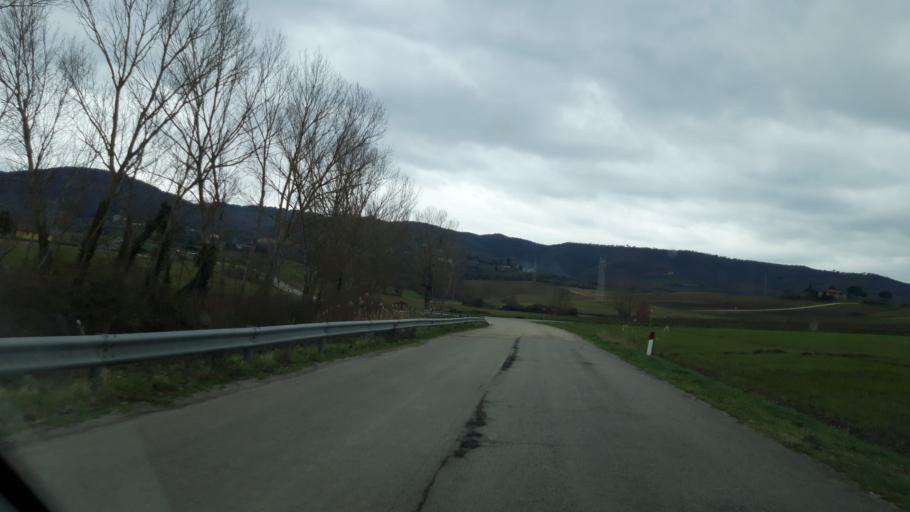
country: IT
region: Umbria
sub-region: Provincia di Perugia
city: Fontignano
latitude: 42.9906
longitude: 12.1821
